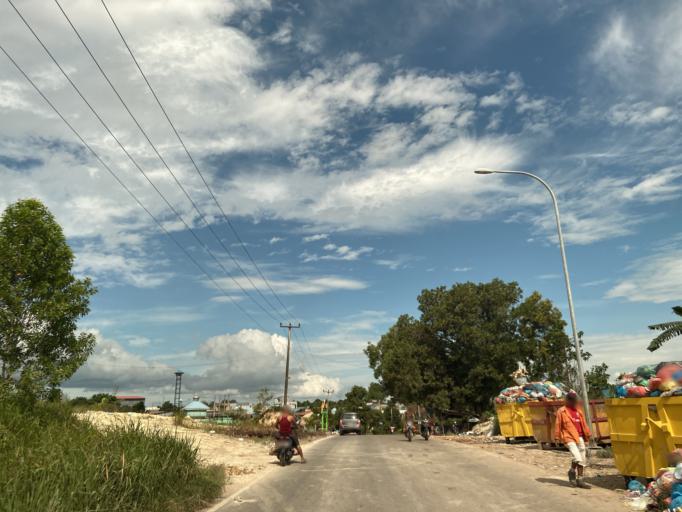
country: SG
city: Singapore
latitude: 1.0303
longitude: 103.9428
